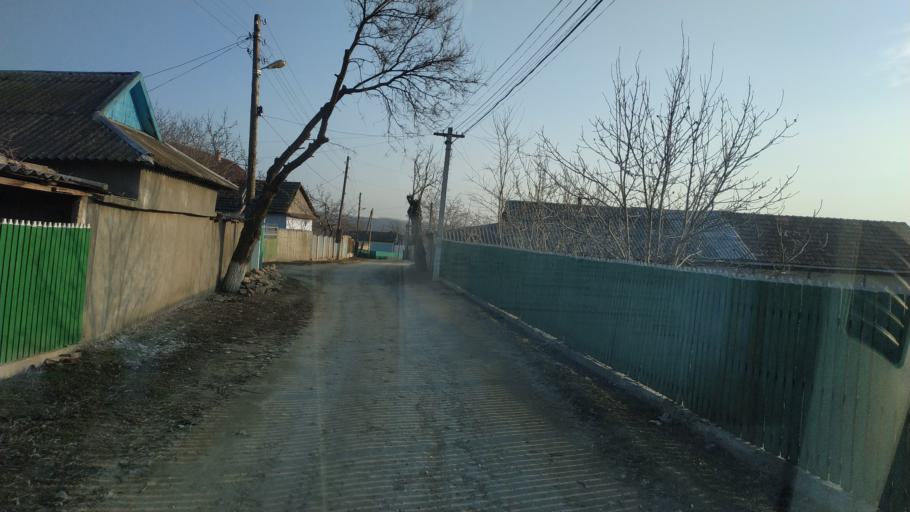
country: MD
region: Hincesti
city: Dancu
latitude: 46.7714
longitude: 28.3539
